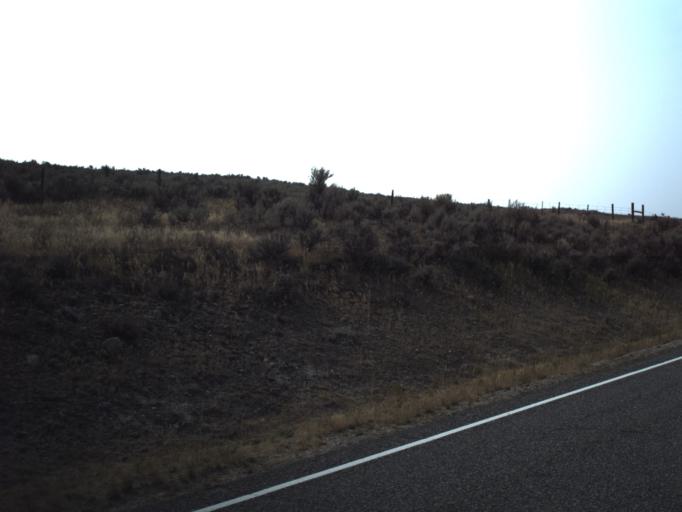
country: US
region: Utah
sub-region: Morgan County
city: Morgan
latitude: 40.9583
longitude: -111.5484
